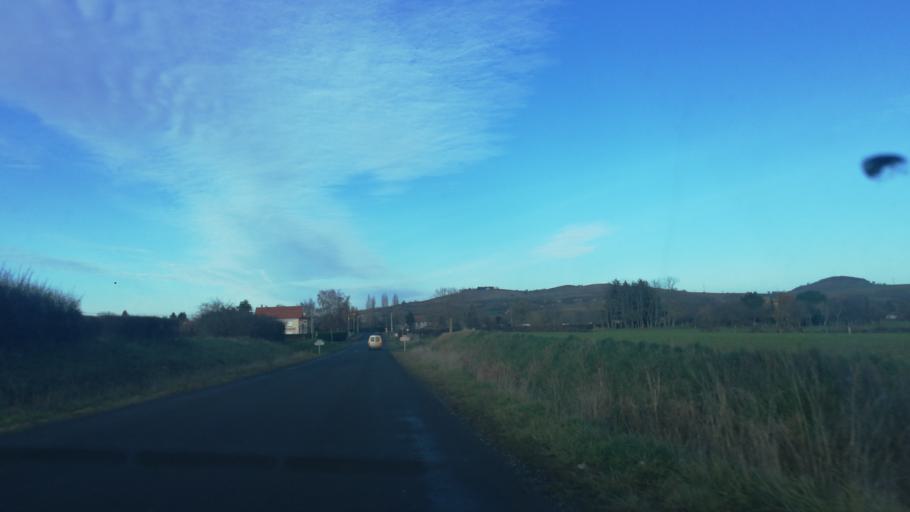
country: FR
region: Auvergne
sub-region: Departement du Puy-de-Dome
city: Billom
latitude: 45.7198
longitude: 3.3497
